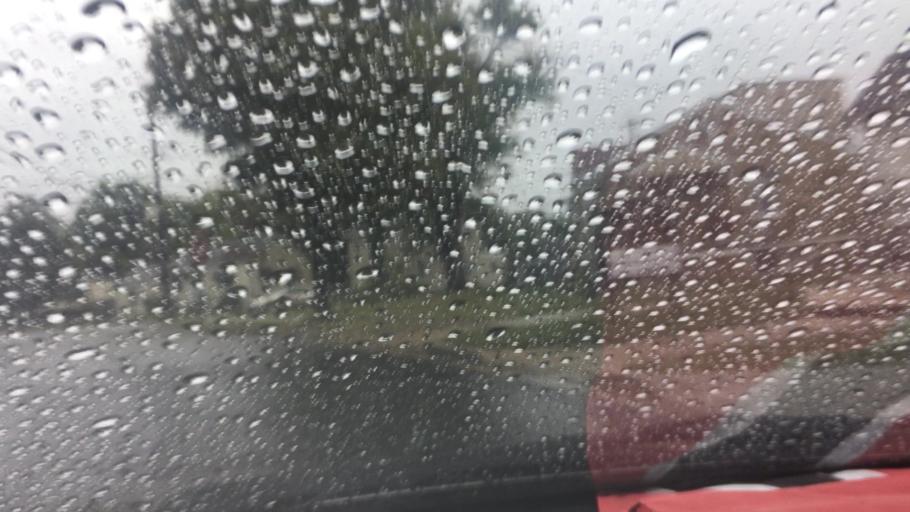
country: US
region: Maryland
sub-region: Prince George's County
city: Fairmount Heights
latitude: 38.9066
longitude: -76.9189
